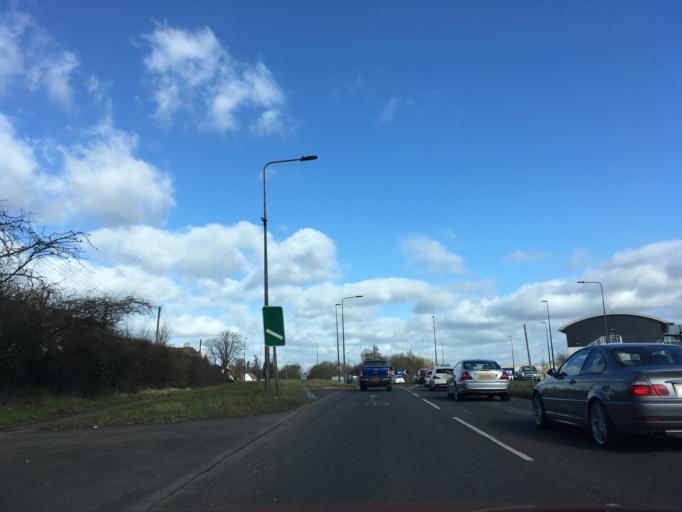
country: GB
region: England
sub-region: South Gloucestershire
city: Almondsbury
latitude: 51.5241
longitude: -2.6164
